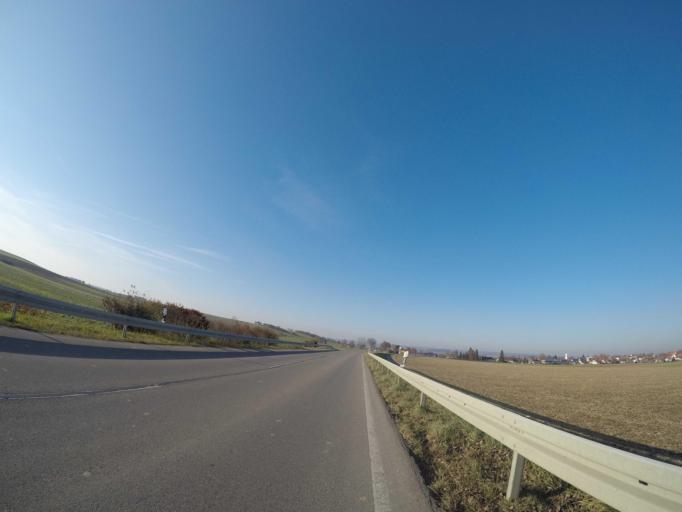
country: DE
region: Baden-Wuerttemberg
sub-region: Tuebingen Region
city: Unterstadion
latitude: 48.1962
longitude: 9.6870
